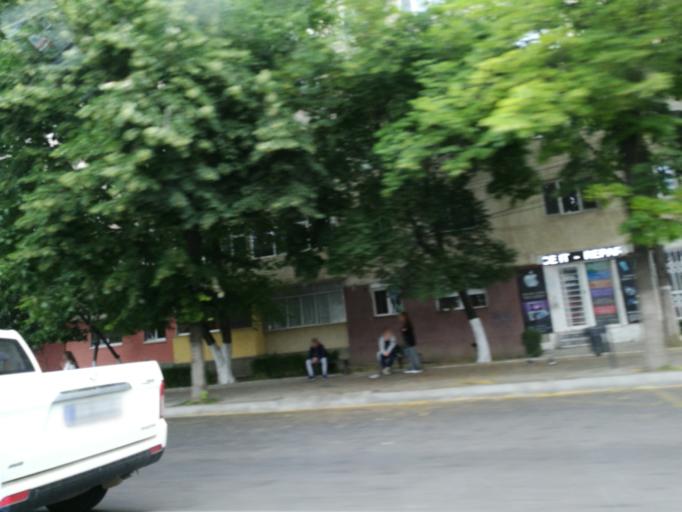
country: RO
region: Constanta
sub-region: Municipiul Constanta
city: Constanta
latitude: 44.1806
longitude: 28.6360
